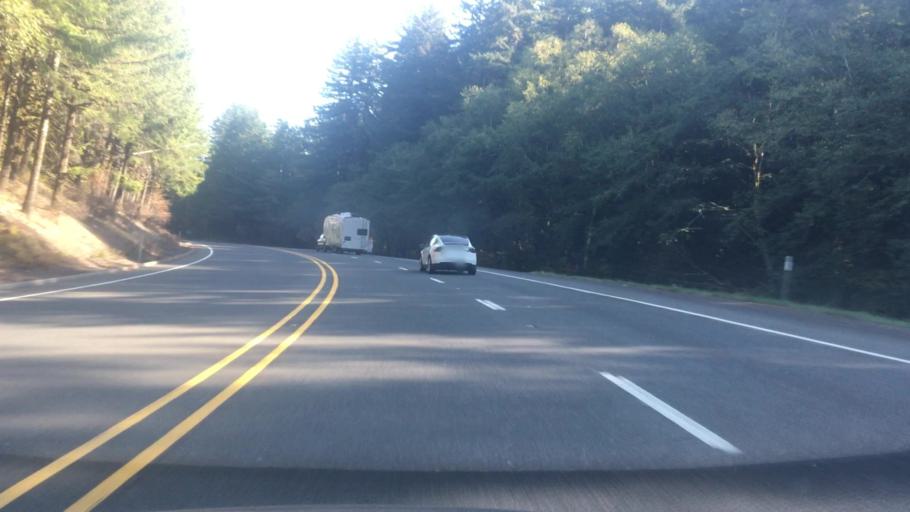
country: US
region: Oregon
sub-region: Polk County
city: Grand Ronde
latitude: 45.0606
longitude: -123.6999
